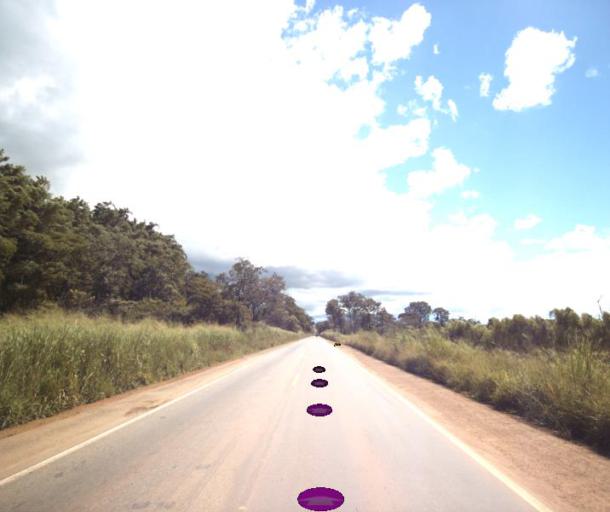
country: BR
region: Goias
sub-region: Anapolis
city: Anapolis
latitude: -16.1499
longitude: -49.0450
